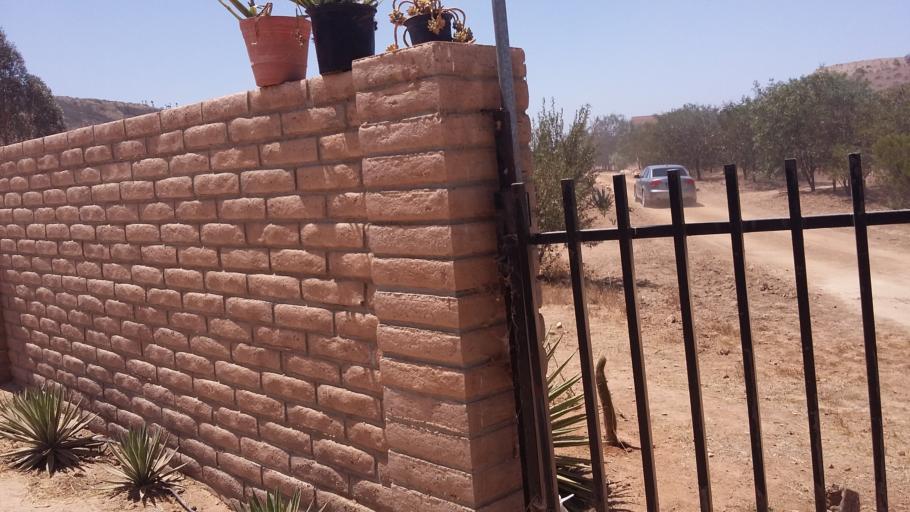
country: MX
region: Baja California
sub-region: Ensenada
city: Rancho Verde
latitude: 32.0330
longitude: -116.6250
